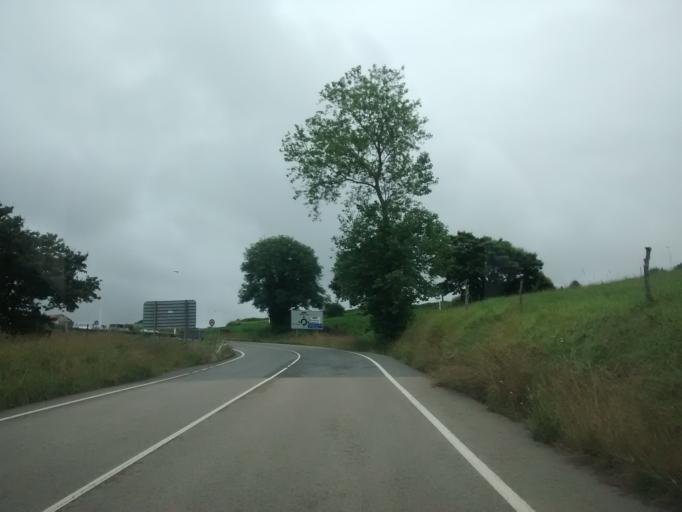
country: ES
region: Cantabria
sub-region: Provincia de Cantabria
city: Santillana
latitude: 43.3933
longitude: -4.1152
